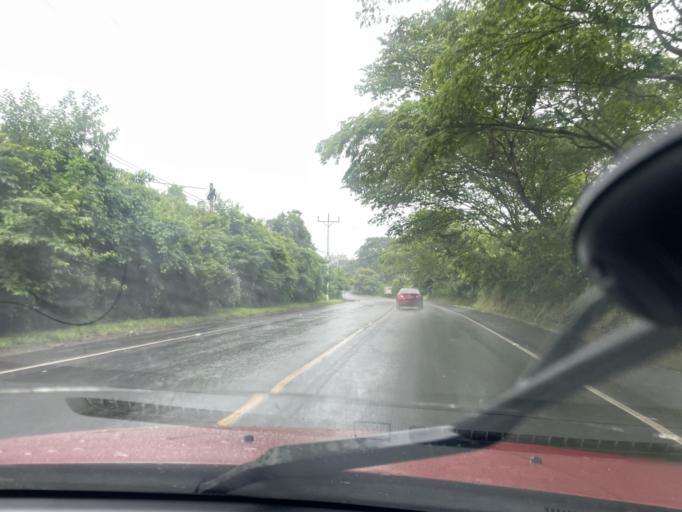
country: SV
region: Morazan
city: Jocoro
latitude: 13.5706
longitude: -88.0884
